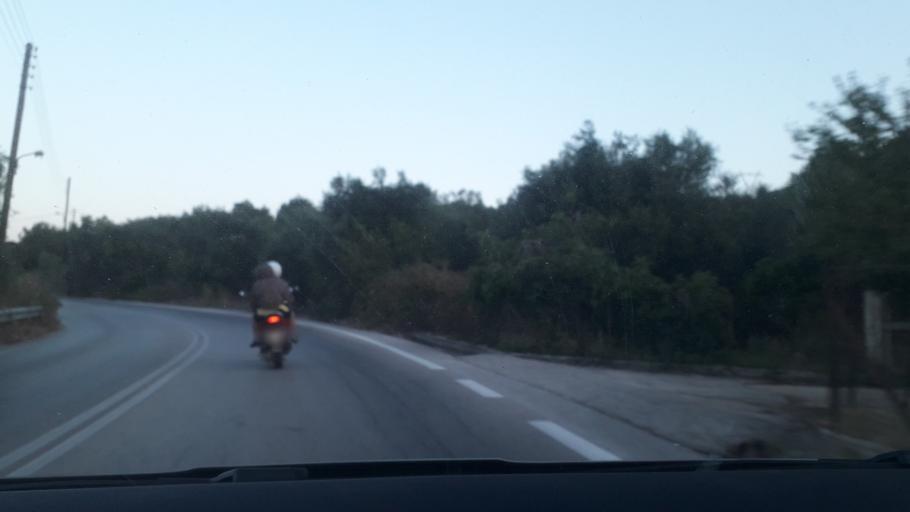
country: GR
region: Ionian Islands
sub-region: Nomos Kerkyras
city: Agios Matthaios
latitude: 39.4549
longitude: 19.9219
